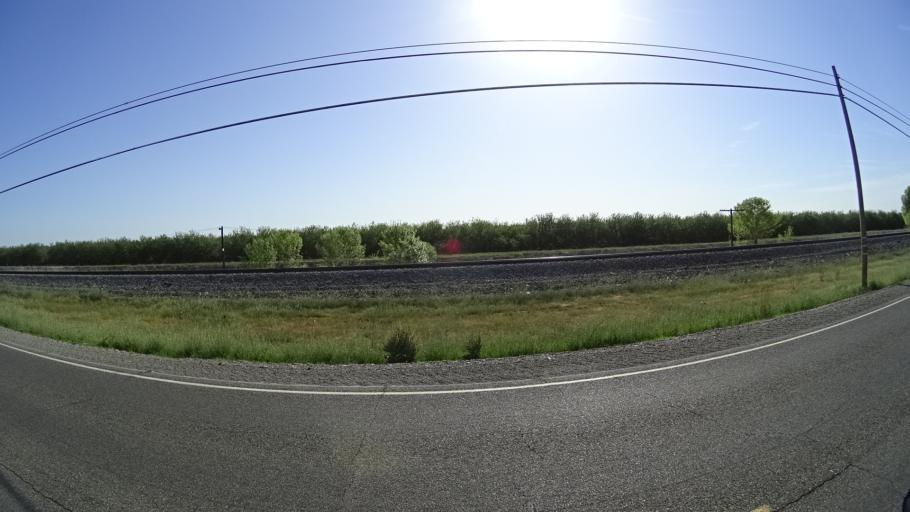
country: US
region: California
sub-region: Glenn County
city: Willows
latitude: 39.5653
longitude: -122.1940
